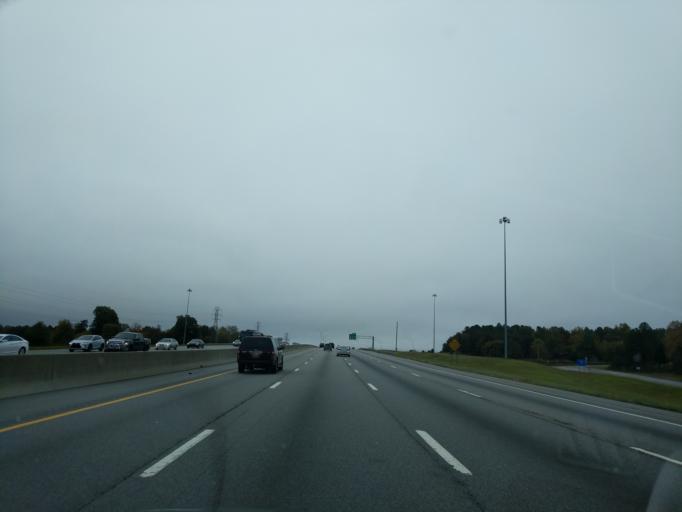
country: US
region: North Carolina
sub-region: Orange County
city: Hillsborough
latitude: 36.0737
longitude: -79.1729
